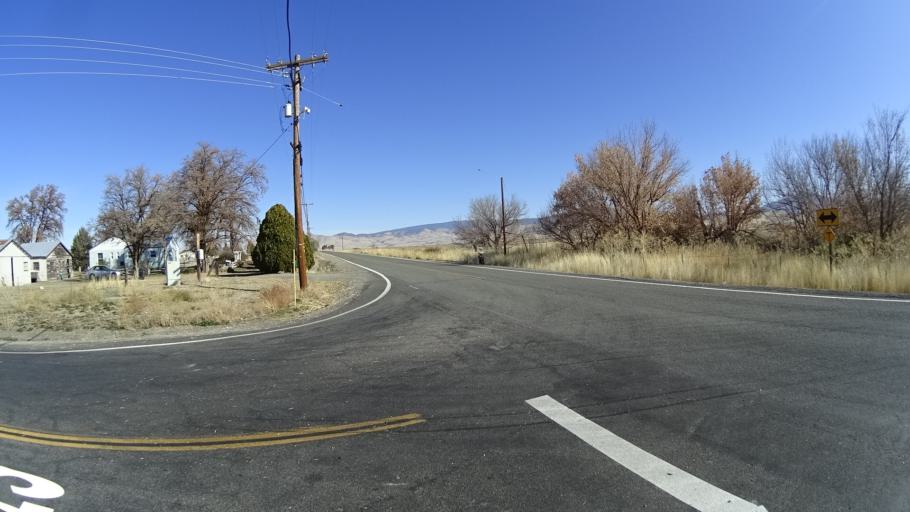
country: US
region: California
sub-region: Siskiyou County
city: Montague
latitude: 41.7704
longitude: -122.4810
